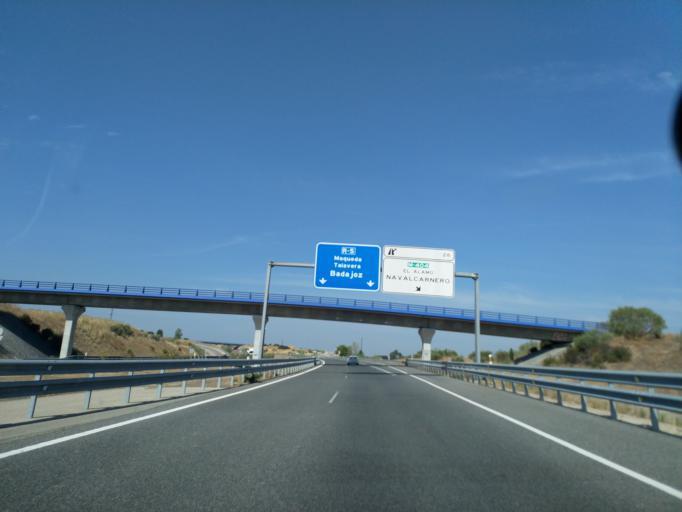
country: ES
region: Madrid
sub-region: Provincia de Madrid
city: Navalcarnero
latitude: 40.2654
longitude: -4.0003
